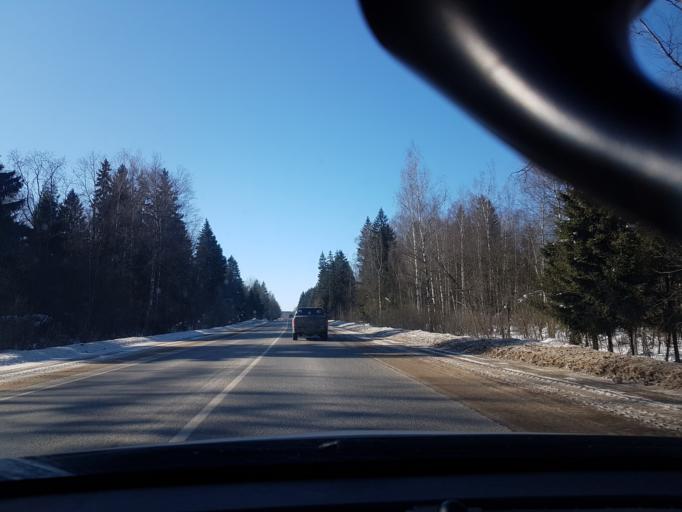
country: RU
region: Moskovskaya
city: Kostrovo
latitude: 55.9132
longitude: 36.7075
